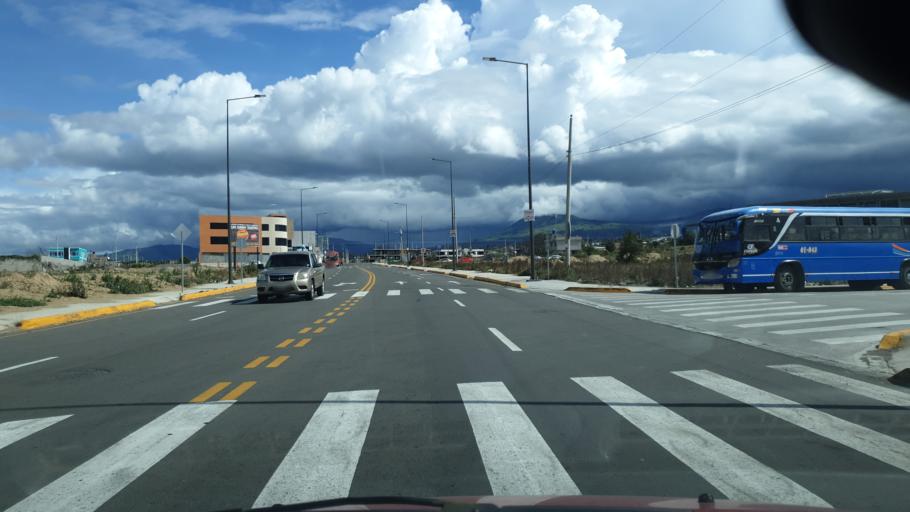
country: EC
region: Tungurahua
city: Ambato
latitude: -1.2981
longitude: -78.6317
